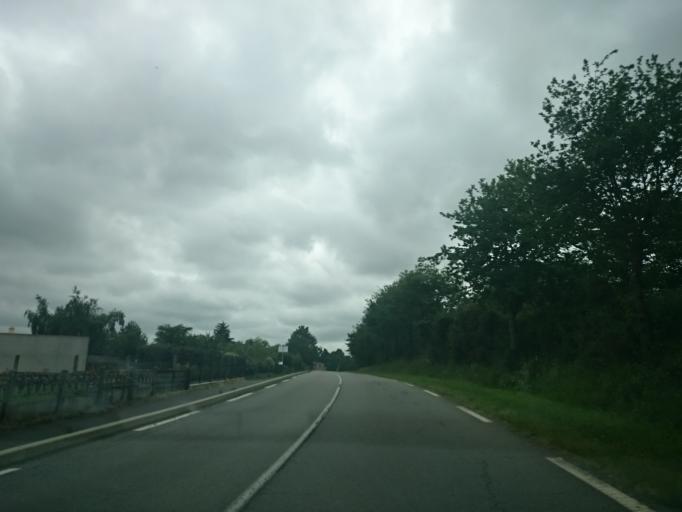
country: FR
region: Pays de la Loire
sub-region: Departement de la Loire-Atlantique
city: Bouaye
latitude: 47.1418
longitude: -1.7068
